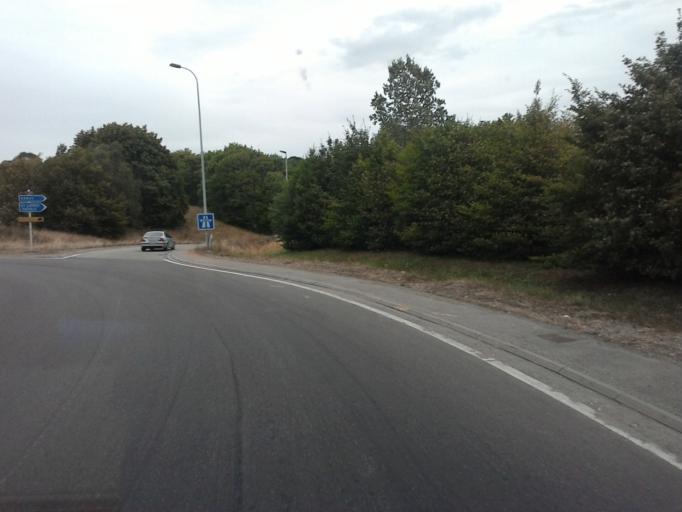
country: FR
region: Lorraine
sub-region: Departement de Meurthe-et-Moselle
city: Richardmenil
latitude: 48.6088
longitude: 6.1739
